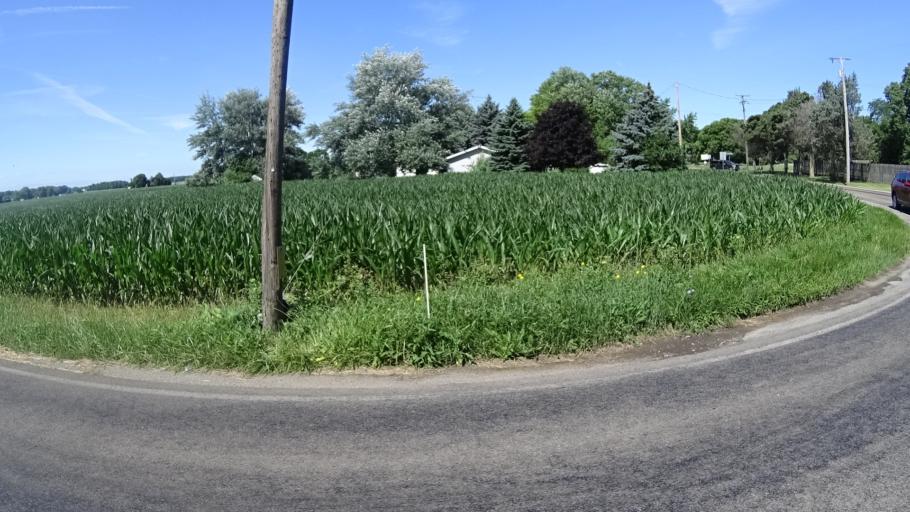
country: US
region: Ohio
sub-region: Ottawa County
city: Port Clinton
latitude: 41.4377
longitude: -82.8419
